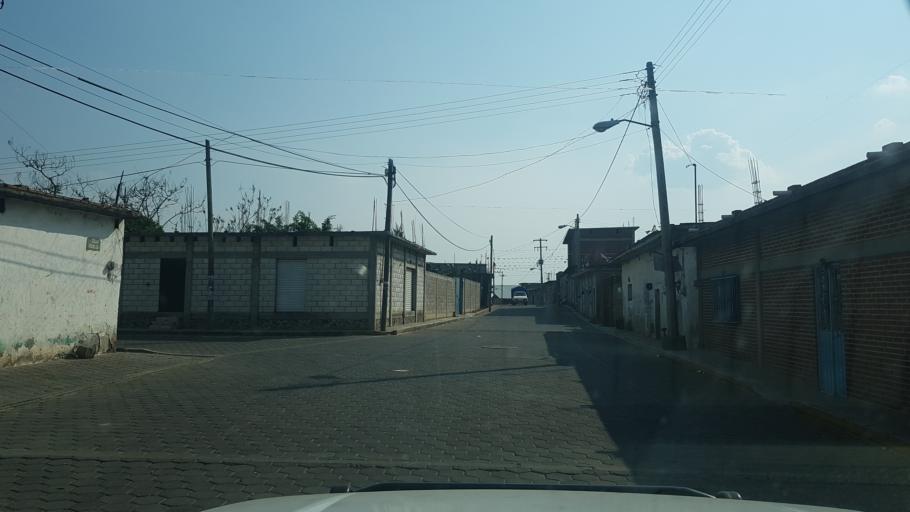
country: MX
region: Morelos
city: Tlacotepec
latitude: 18.7828
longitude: -98.7218
